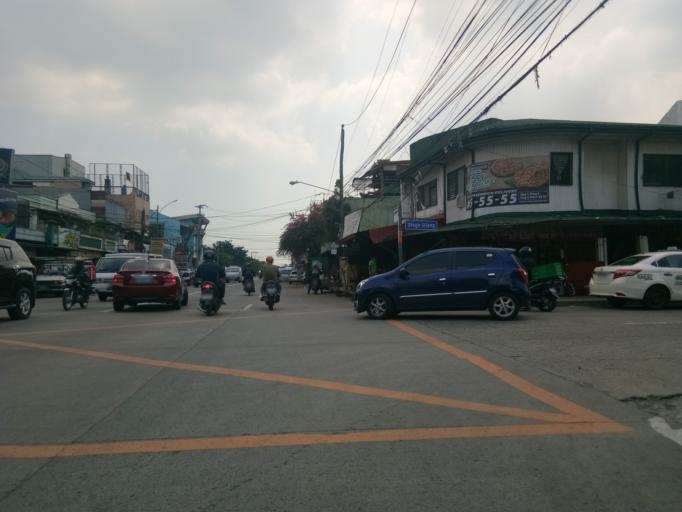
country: PH
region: Metro Manila
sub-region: Marikina
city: Calumpang
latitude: 14.6188
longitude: 121.0640
